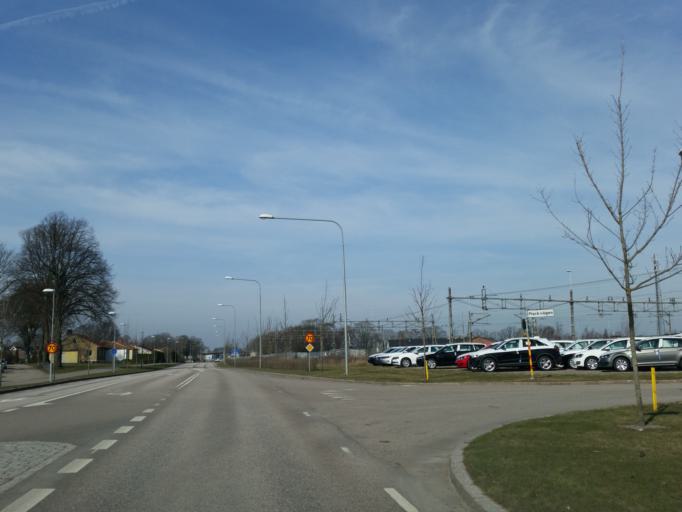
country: SE
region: Kalmar
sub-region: Kalmar Kommun
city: Kalmar
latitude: 56.6670
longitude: 16.3268
